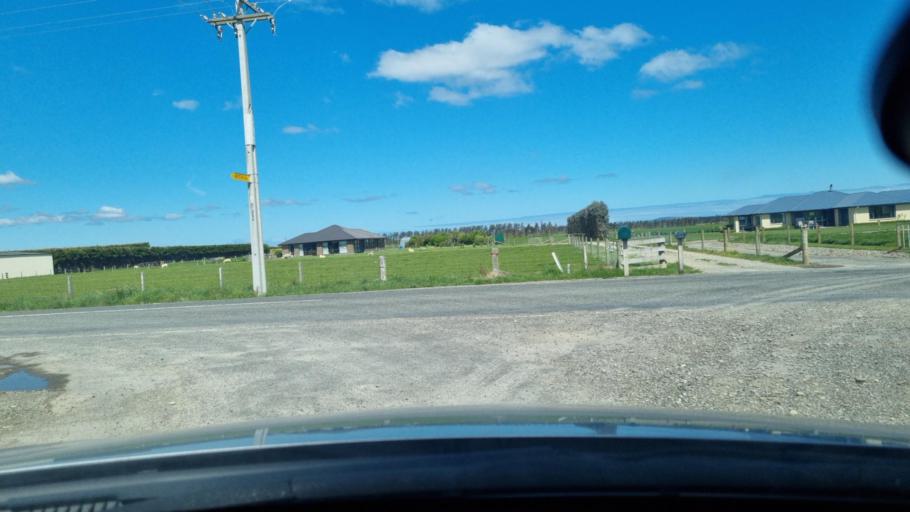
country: NZ
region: Southland
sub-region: Invercargill City
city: Invercargill
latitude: -46.3689
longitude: 168.2826
